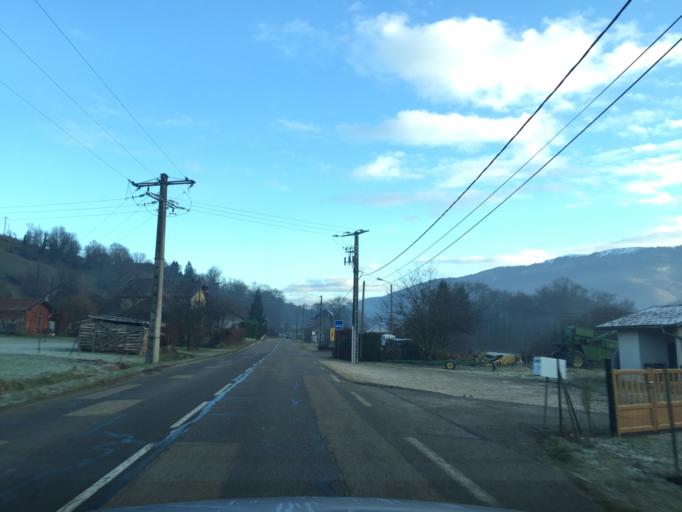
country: FR
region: Rhone-Alpes
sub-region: Departement de la Haute-Savoie
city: Cusy
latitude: 45.7550
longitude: 6.0024
